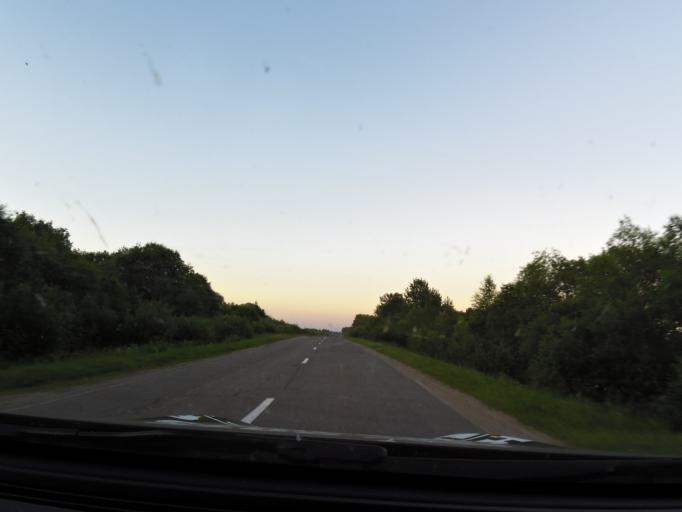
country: RU
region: Jaroslavl
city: Lyubim
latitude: 58.3232
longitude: 41.0231
